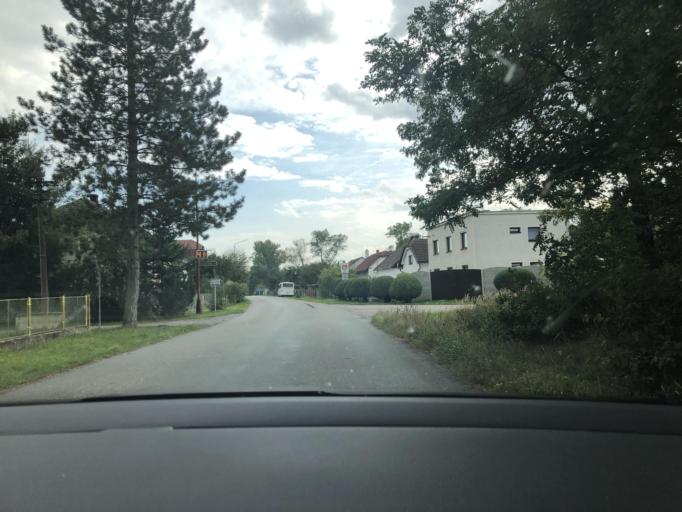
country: CZ
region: Pardubicky
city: Recany nad Labem
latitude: 50.0627
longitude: 15.4832
